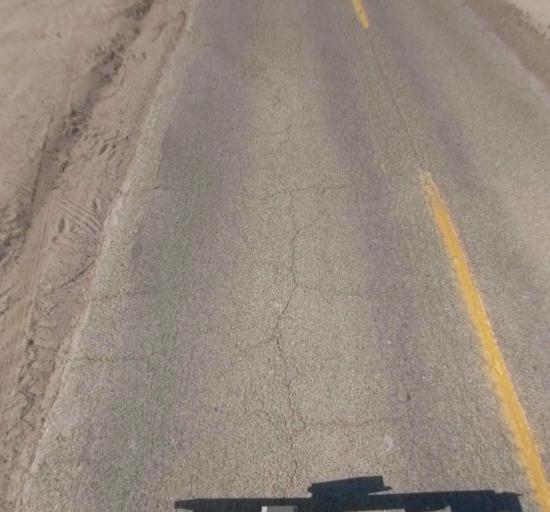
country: US
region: California
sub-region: Madera County
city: Parkwood
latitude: 36.8536
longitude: -120.1284
